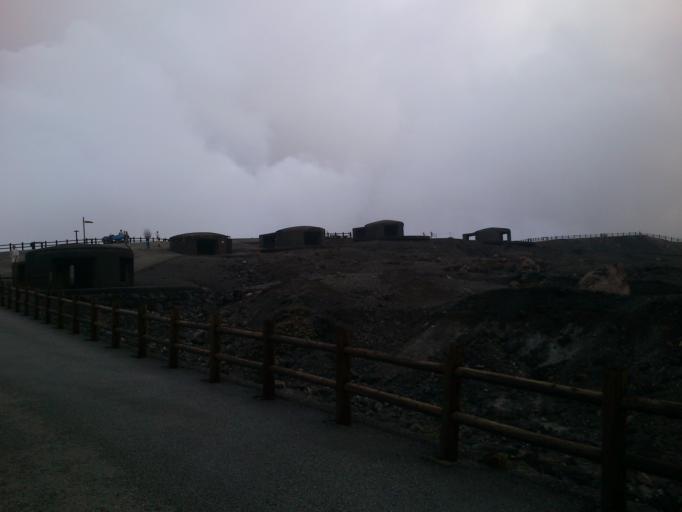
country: JP
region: Kumamoto
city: Aso
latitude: 32.8807
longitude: 131.0844
